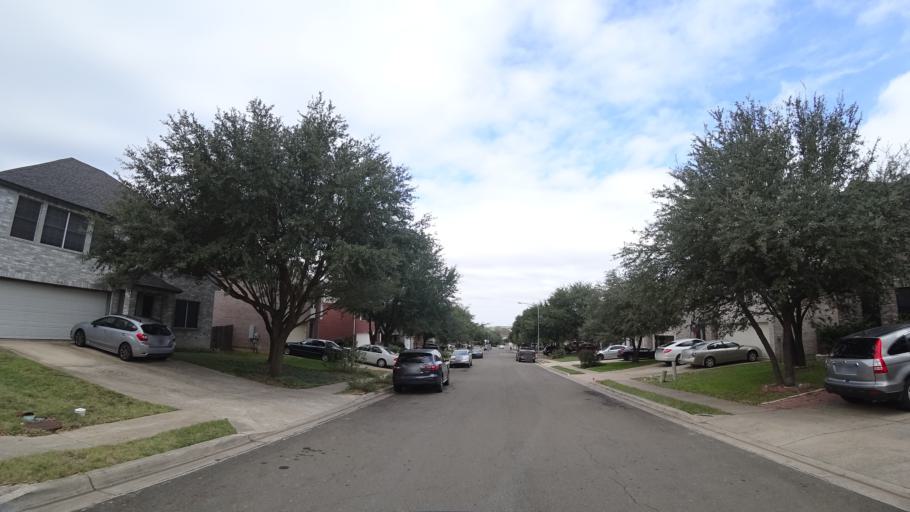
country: US
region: Texas
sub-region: Travis County
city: Manchaca
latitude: 30.1564
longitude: -97.8427
